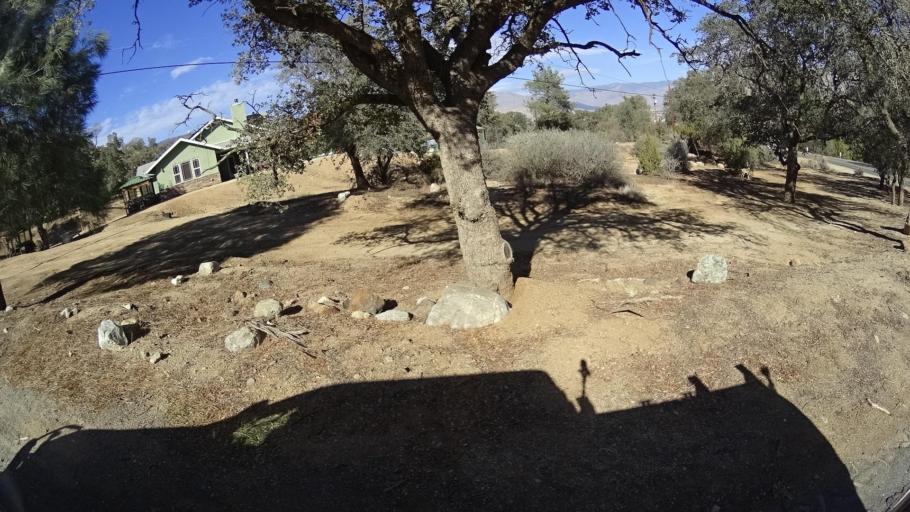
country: US
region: California
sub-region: Kern County
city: Bodfish
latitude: 35.5849
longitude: -118.4982
